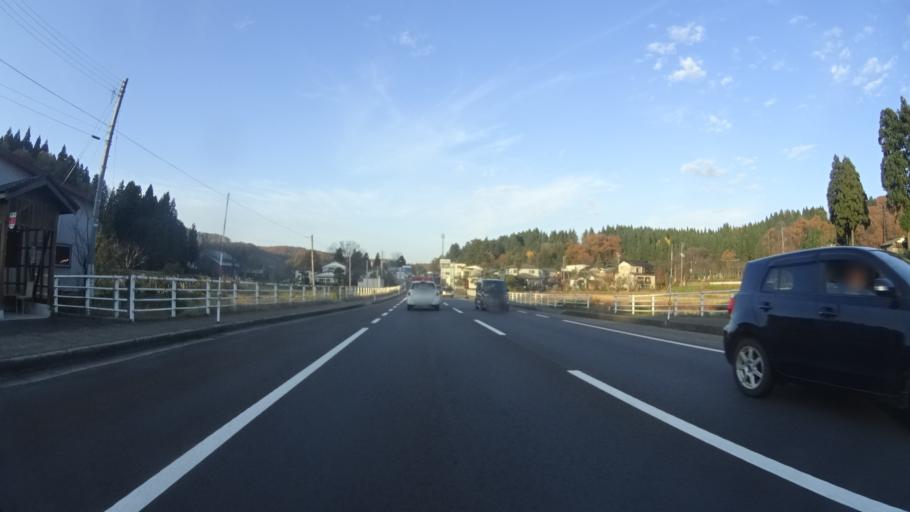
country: JP
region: Niigata
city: Nagaoka
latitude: 37.4296
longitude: 138.7270
